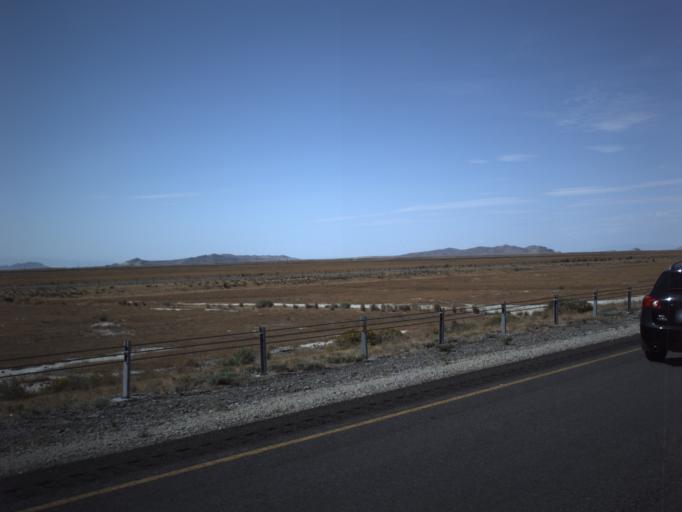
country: US
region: Utah
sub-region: Tooele County
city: Grantsville
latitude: 40.7261
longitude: -113.1556
